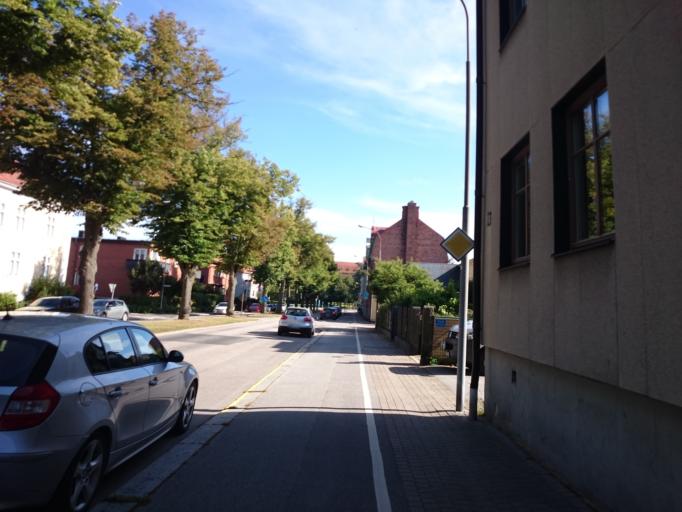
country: SE
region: Blekinge
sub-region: Karlshamns Kommun
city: Karlshamn
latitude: 56.1680
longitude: 14.8704
